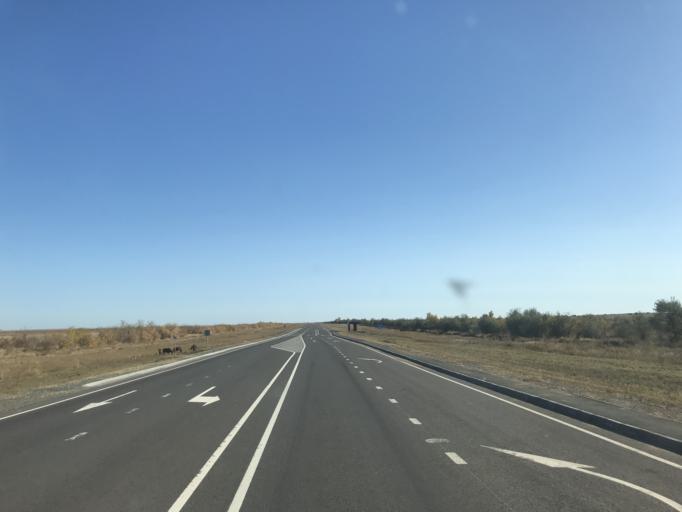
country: KZ
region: Pavlodar
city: Aksu
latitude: 52.0629
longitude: 77.1649
